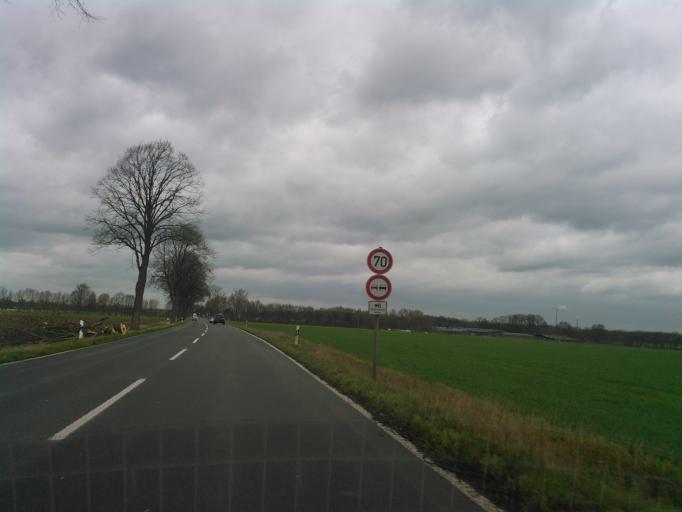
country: DE
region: North Rhine-Westphalia
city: Marl
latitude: 51.6325
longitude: 7.0850
